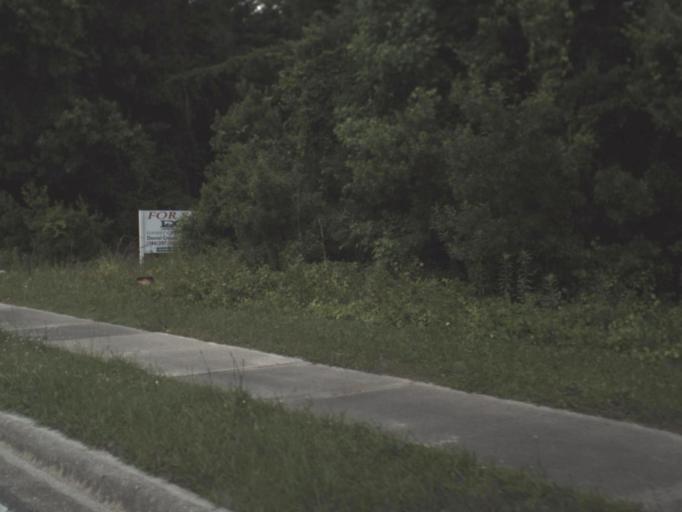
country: US
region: Florida
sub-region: Columbia County
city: Five Points
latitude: 30.2364
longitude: -82.6385
